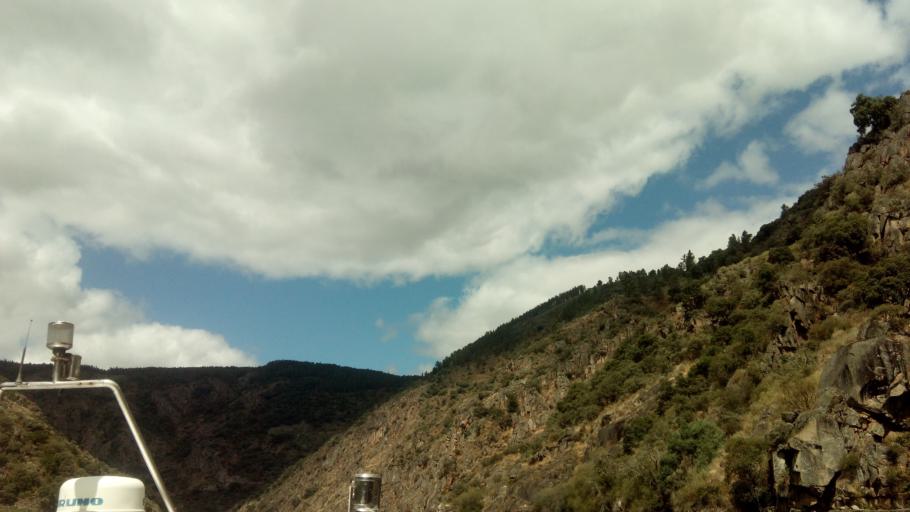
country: ES
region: Galicia
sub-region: Provincia de Lugo
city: Lobios
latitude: 42.3987
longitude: -7.5620
